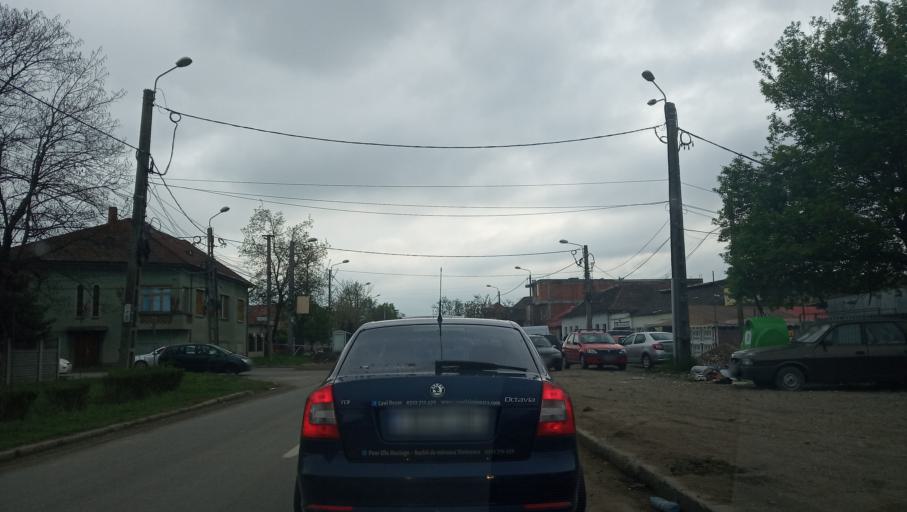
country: RO
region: Timis
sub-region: Comuna Ghiroda
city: Ghiroda
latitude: 45.7643
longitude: 21.2629
